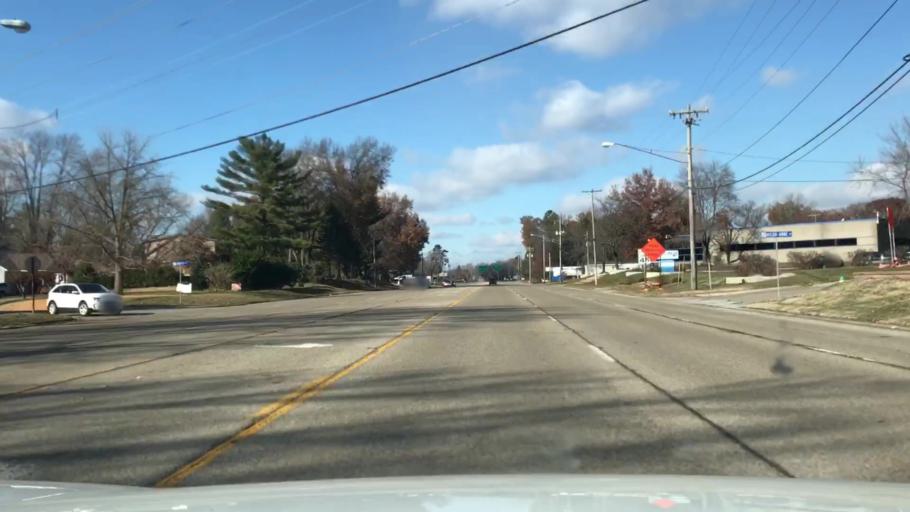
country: US
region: Illinois
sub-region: Saint Clair County
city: Swansea
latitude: 38.5377
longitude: -89.9926
